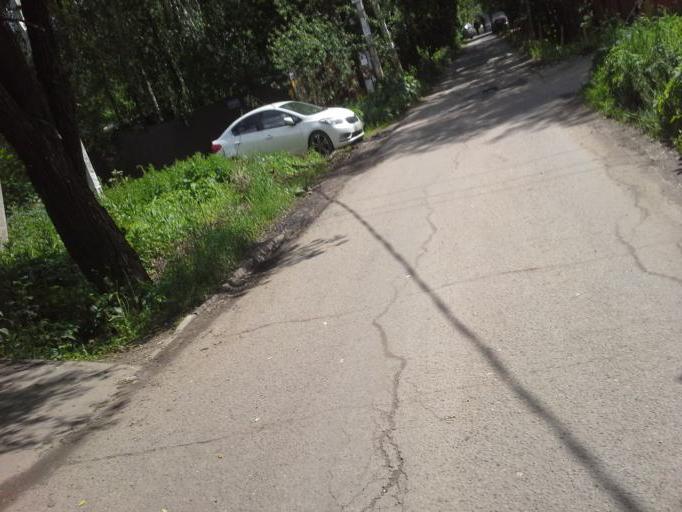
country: RU
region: Moskovskaya
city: Lesnoy Gorodok
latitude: 55.6308
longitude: 37.2140
